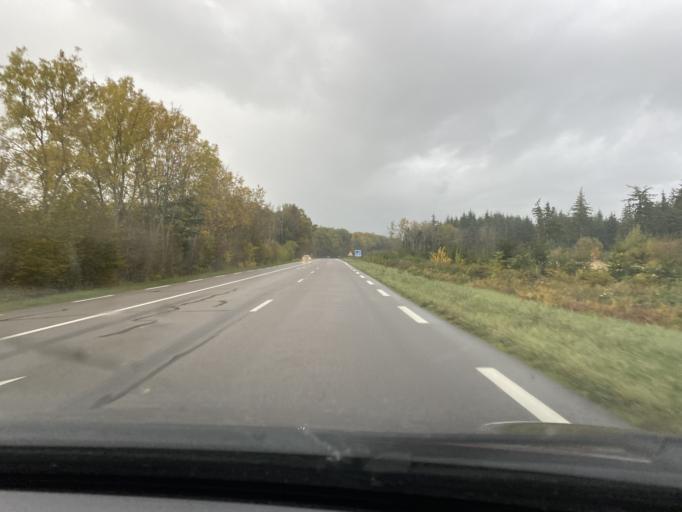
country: FR
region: Bourgogne
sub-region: Departement de la Cote-d'Or
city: Saulieu
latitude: 47.3312
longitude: 4.1930
